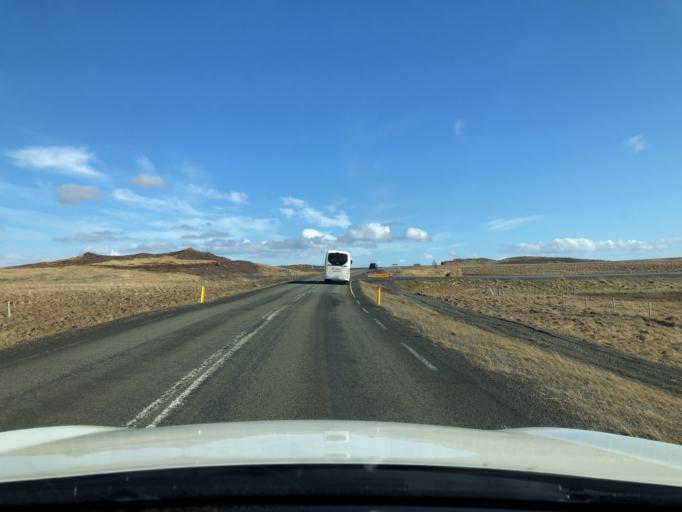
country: IS
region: West
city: Borgarnes
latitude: 64.5543
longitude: -21.7321
